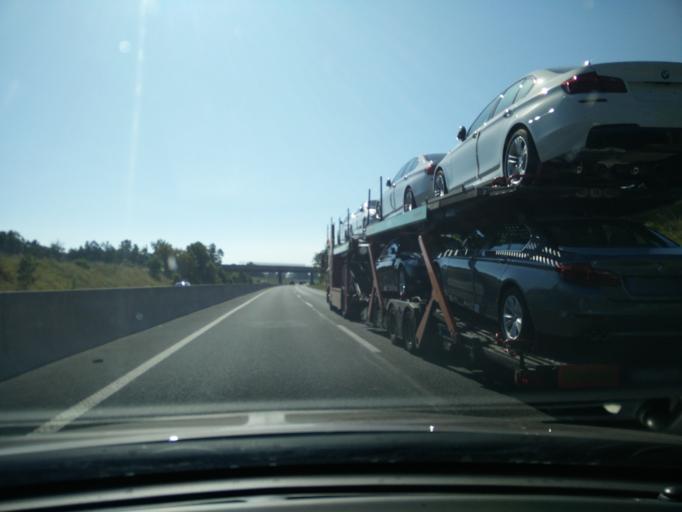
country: SI
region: Radovljica
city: Lesce
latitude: 46.3818
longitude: 14.1474
